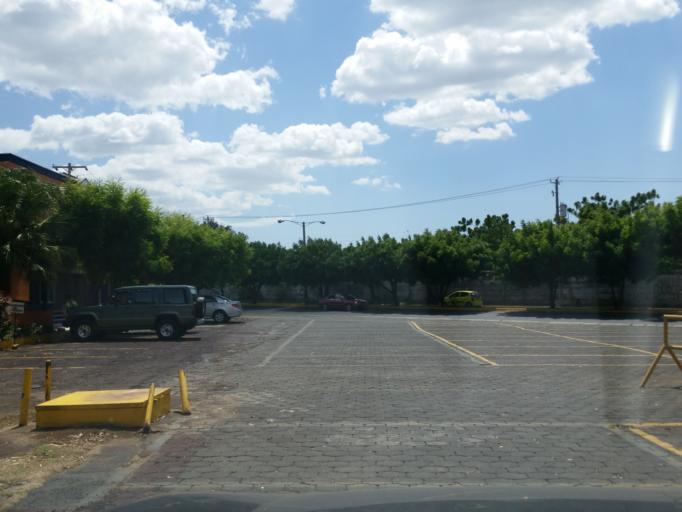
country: NI
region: Managua
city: Managua
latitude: 12.1177
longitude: -86.2477
